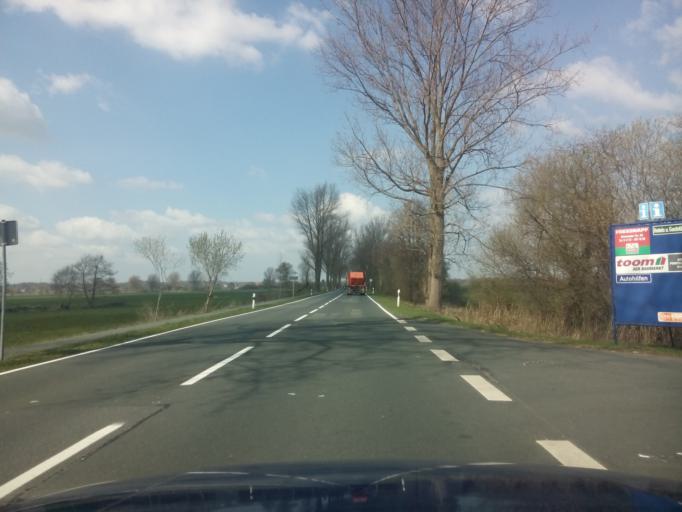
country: DE
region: Lower Saxony
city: Osterholz-Scharmbeck
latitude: 53.2054
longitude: 8.8202
